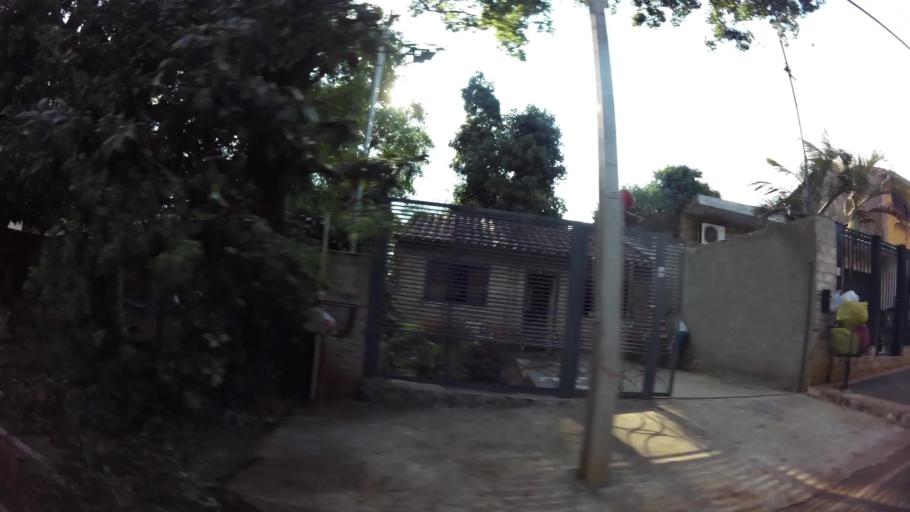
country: PY
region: Central
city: Fernando de la Mora
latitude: -25.3557
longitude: -57.5545
